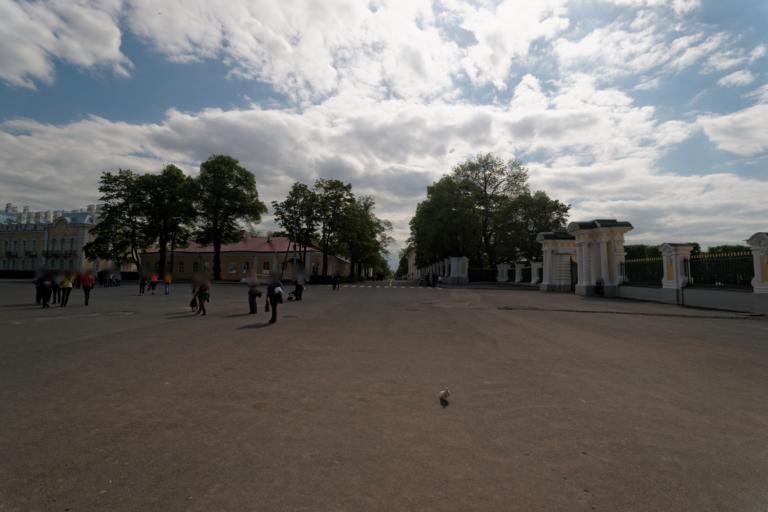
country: RU
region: St.-Petersburg
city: Peterhof
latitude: 59.8843
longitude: 29.9115
